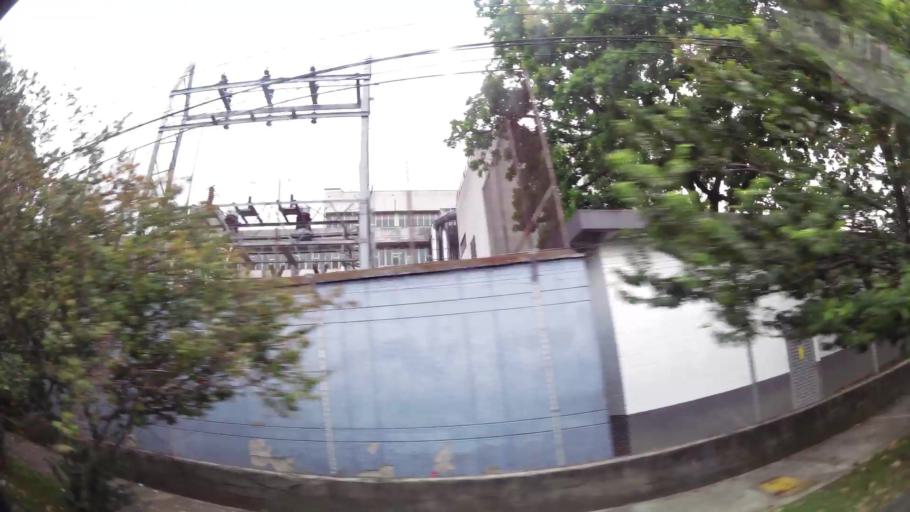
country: CO
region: Antioquia
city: Itagui
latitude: 6.2093
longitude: -75.5801
